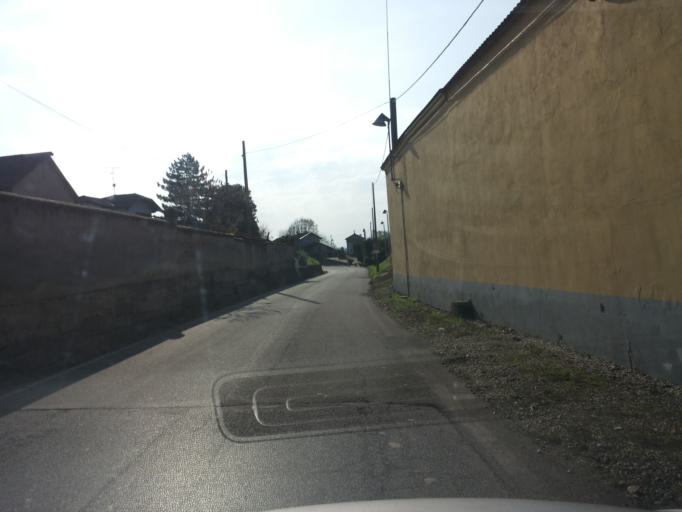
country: IT
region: Piedmont
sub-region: Provincia di Vercelli
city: Pezzana
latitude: 45.2573
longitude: 8.4817
